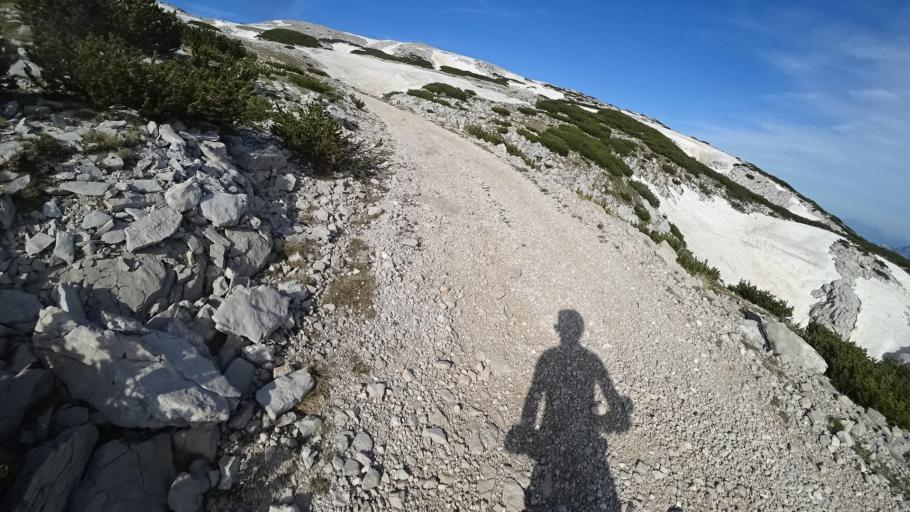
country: BA
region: Federation of Bosnia and Herzegovina
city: Kocerin
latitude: 43.5970
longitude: 17.5448
